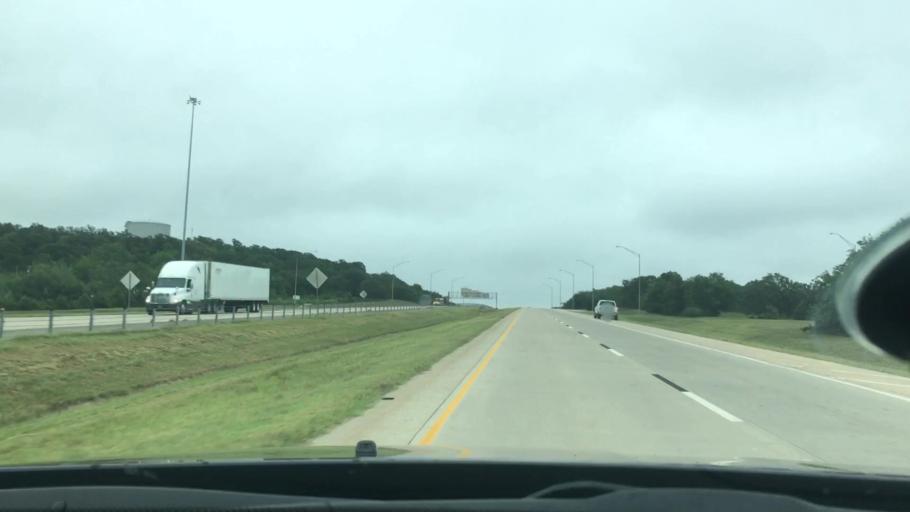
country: US
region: Oklahoma
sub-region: Okmulgee County
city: Henryetta
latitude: 35.4319
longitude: -95.9700
